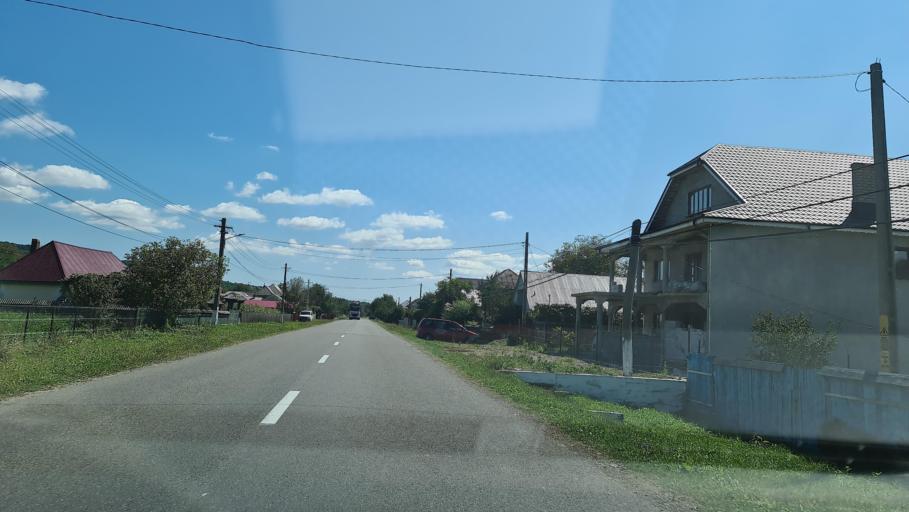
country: RO
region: Bacau
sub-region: Comuna Balcani
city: Balcani
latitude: 46.6512
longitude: 26.5589
